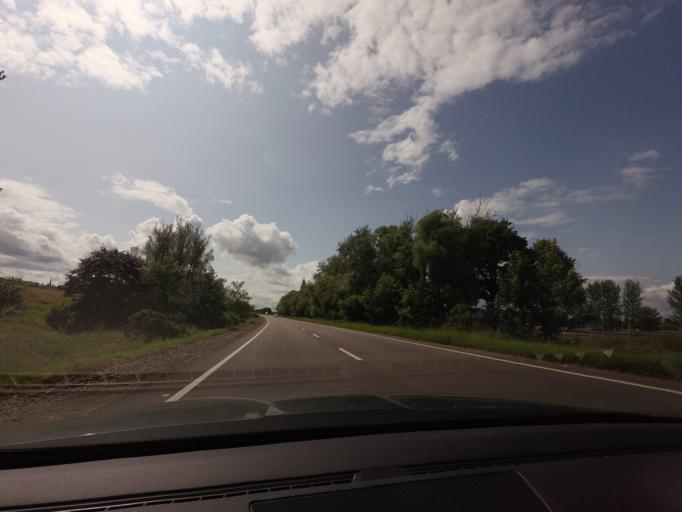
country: GB
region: Scotland
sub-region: Moray
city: Forres
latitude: 57.6147
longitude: -3.6104
